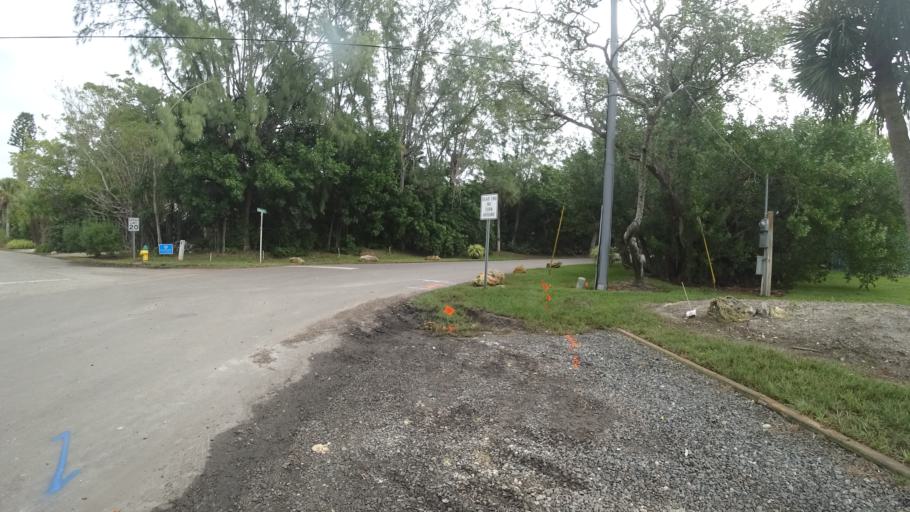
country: US
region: Florida
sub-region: Manatee County
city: Longboat Key
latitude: 27.4266
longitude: -82.6717
